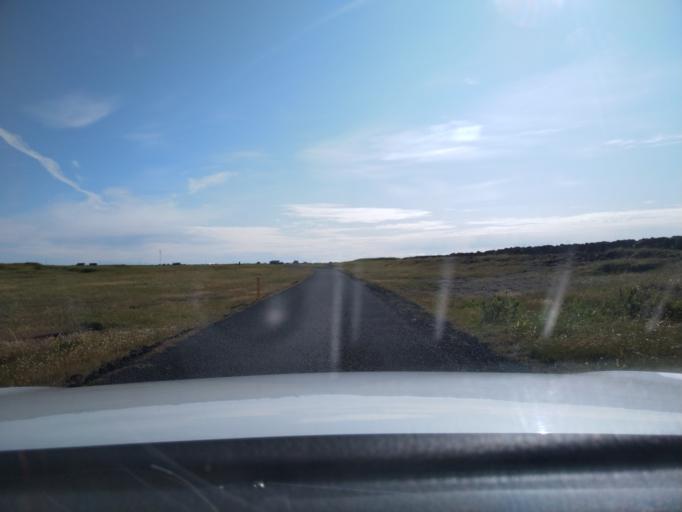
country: IS
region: South
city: THorlakshoefn
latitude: 63.8346
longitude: -21.7022
